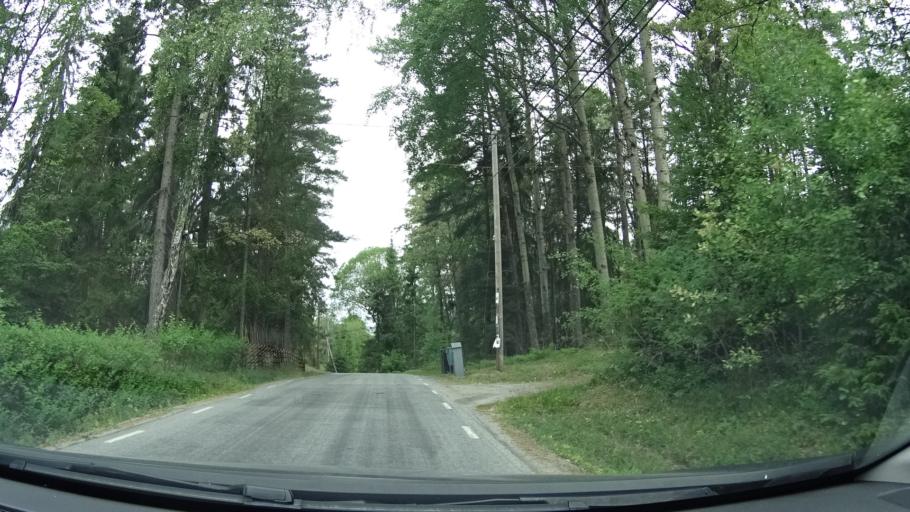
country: SE
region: Stockholm
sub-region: Varmdo Kommun
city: Mortnas
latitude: 59.3725
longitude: 18.4669
